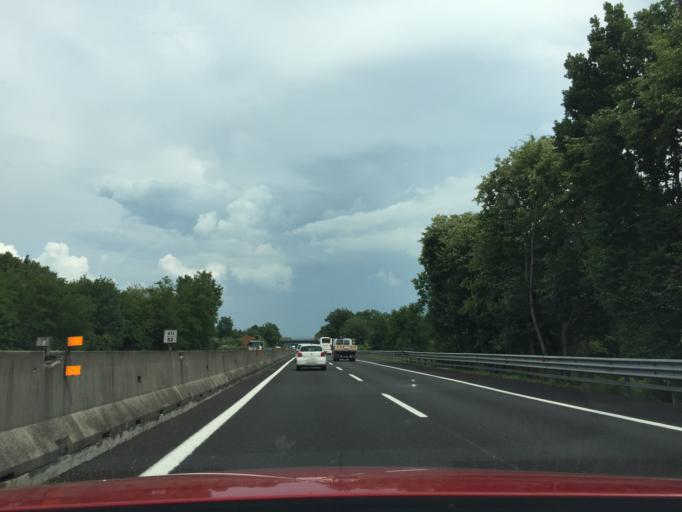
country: IT
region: Tuscany
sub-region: Provincia di Lucca
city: Altopascio
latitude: 43.8164
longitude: 10.6507
